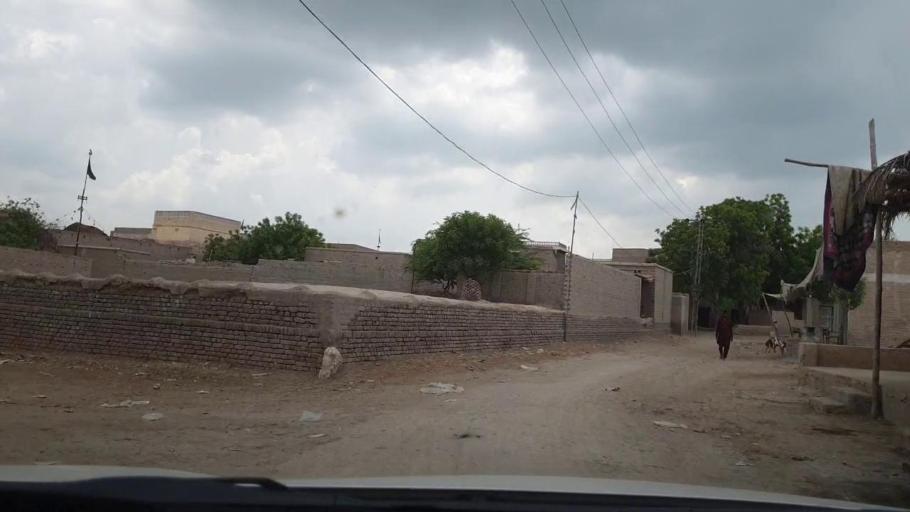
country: PK
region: Sindh
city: Dokri
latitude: 27.3258
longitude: 68.1038
